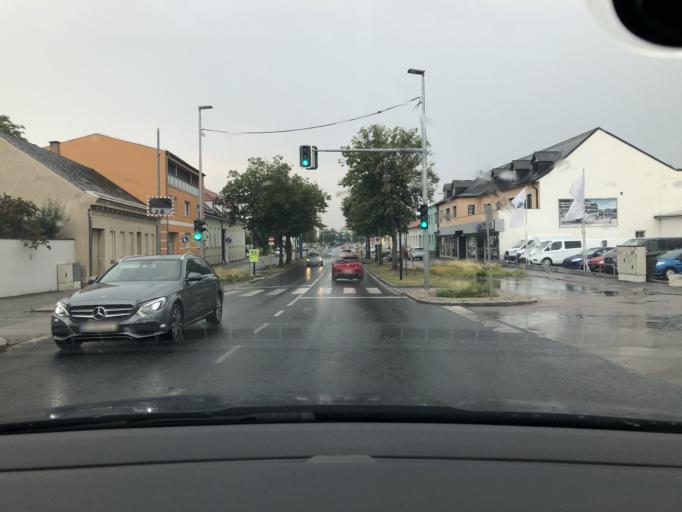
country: AT
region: Lower Austria
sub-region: Politischer Bezirk Ganserndorf
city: Ganserndorf
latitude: 48.3369
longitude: 16.7155
